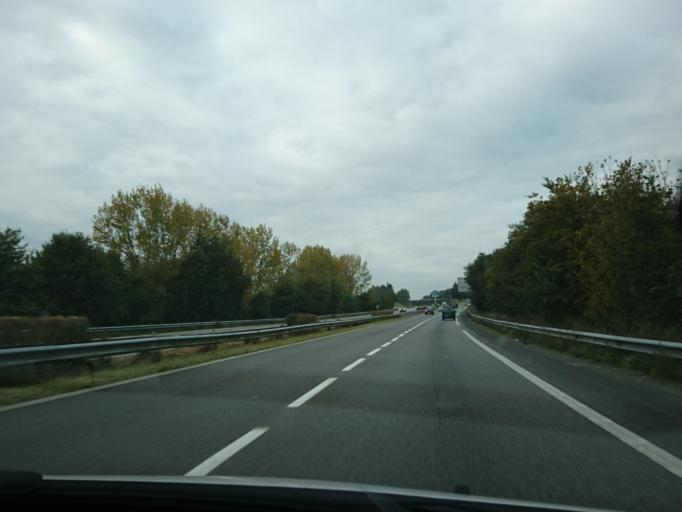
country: FR
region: Pays de la Loire
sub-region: Departement de la Loire-Atlantique
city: Missillac
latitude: 47.4740
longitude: -2.1765
